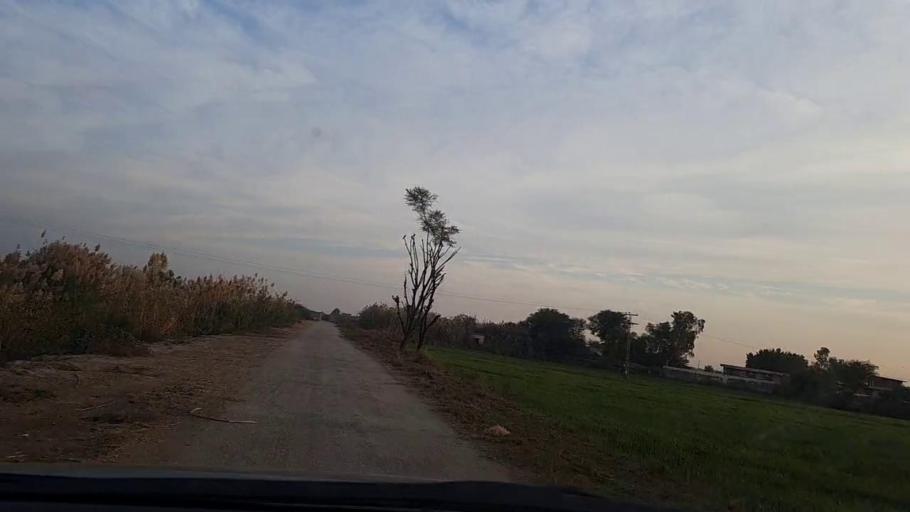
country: PK
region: Sindh
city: Sakrand
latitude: 26.1768
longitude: 68.3435
